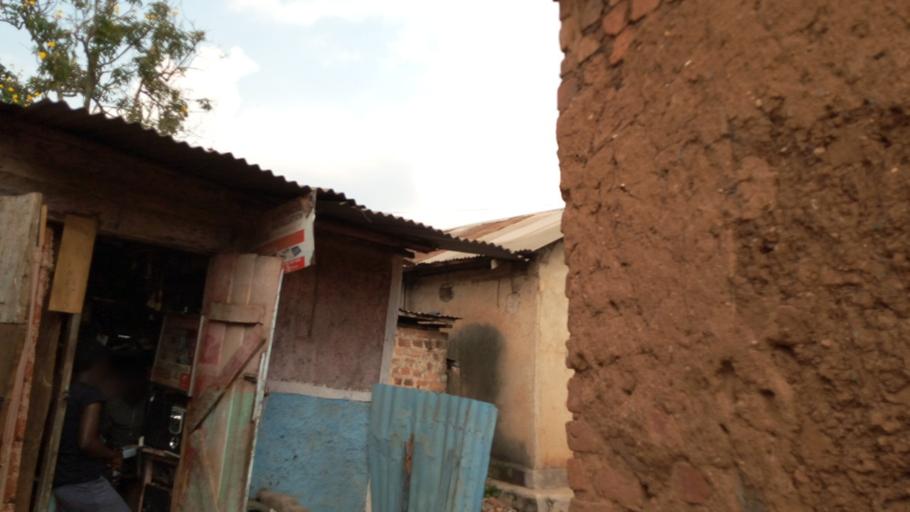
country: UG
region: Central Region
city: Kampala Central Division
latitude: 0.3262
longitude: 32.5676
